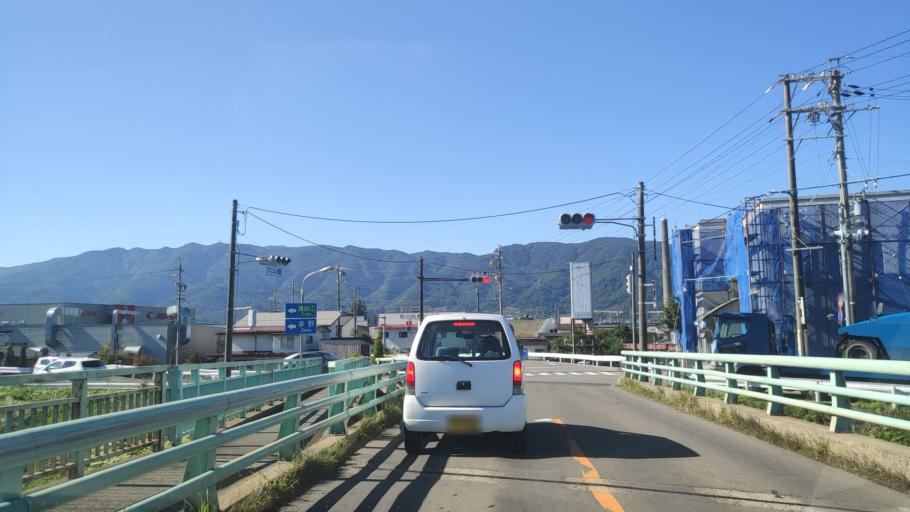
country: JP
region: Nagano
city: Suwa
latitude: 36.0314
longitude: 138.1084
